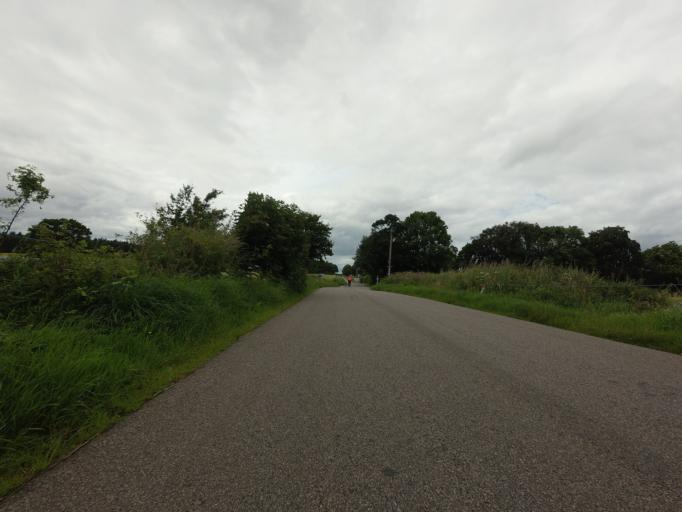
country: GB
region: Scotland
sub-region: Moray
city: Forres
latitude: 57.5992
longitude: -3.7201
